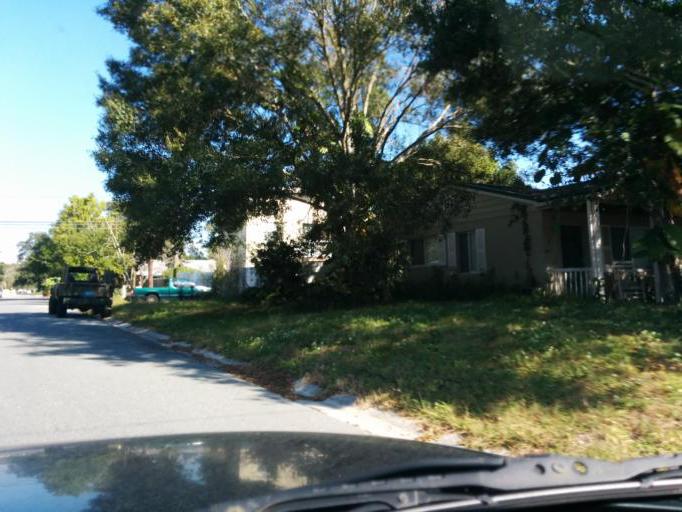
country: US
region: Florida
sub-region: Pinellas County
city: Lealman
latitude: 27.8149
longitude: -82.6427
